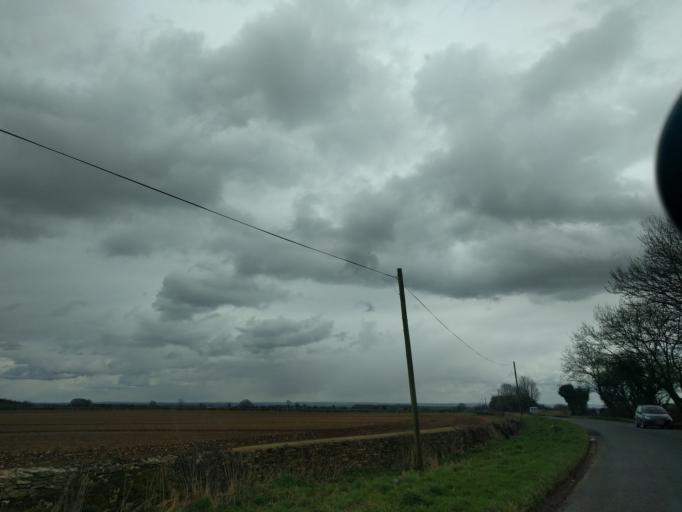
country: GB
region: England
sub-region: Gloucestershire
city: Nailsworth
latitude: 51.6513
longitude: -2.2566
